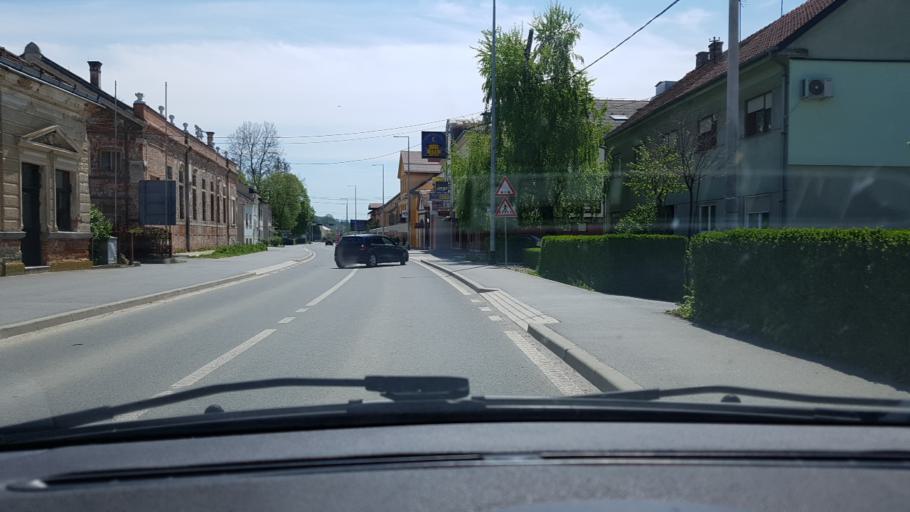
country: HR
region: Krapinsko-Zagorska
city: Zlatar
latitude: 46.0908
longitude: 16.0774
